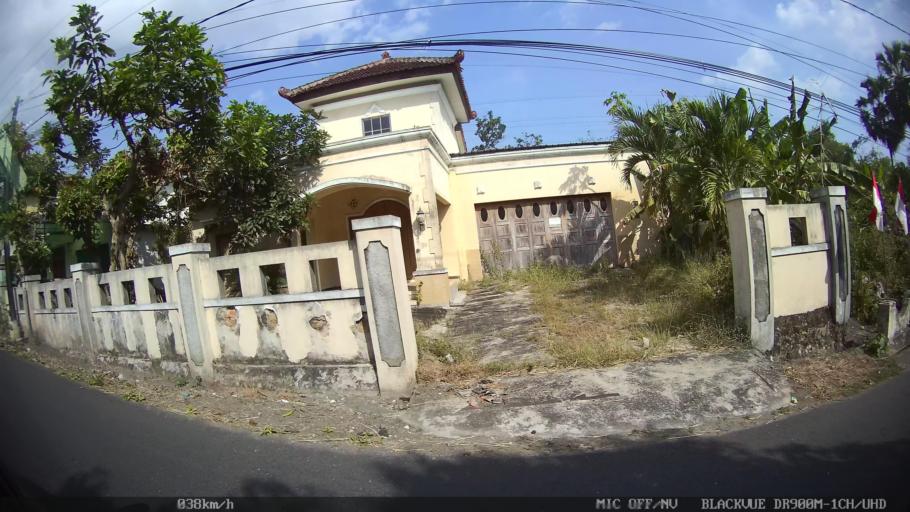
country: ID
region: Daerah Istimewa Yogyakarta
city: Kasihan
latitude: -7.8409
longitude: 110.3120
